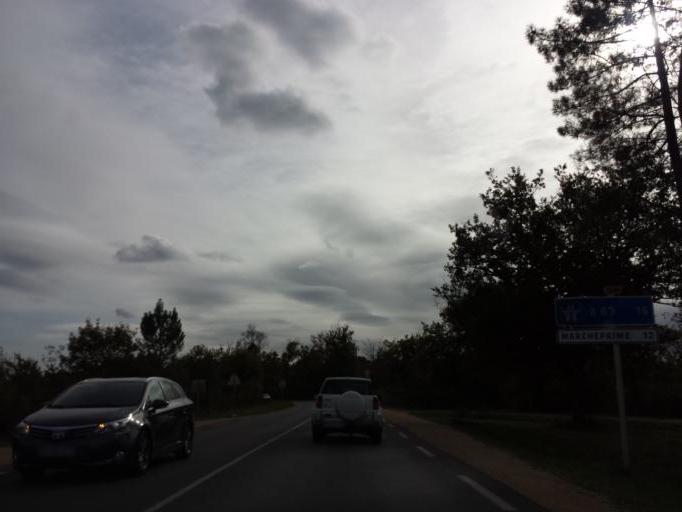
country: FR
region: Aquitaine
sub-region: Departement de la Gironde
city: Marcheprime
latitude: 44.7809
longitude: -0.9318
